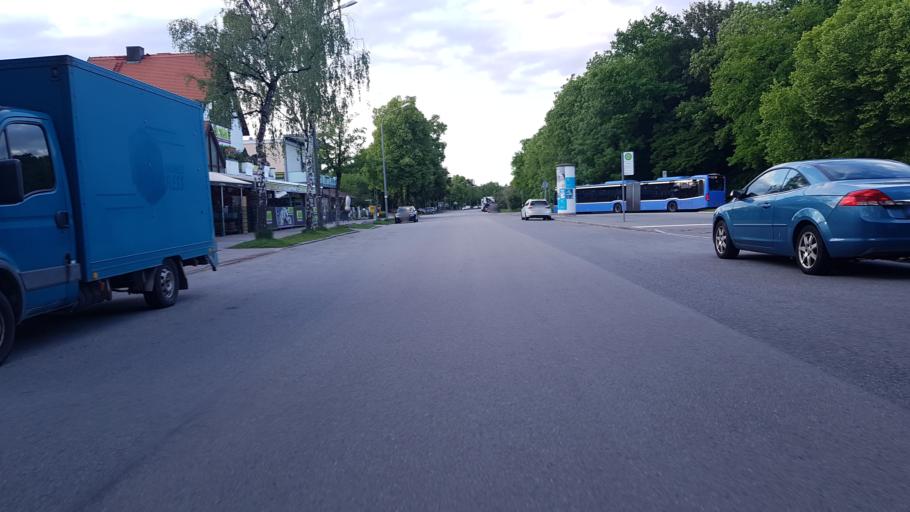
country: DE
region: Bavaria
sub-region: Upper Bavaria
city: Neuried
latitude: 48.1032
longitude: 11.4882
